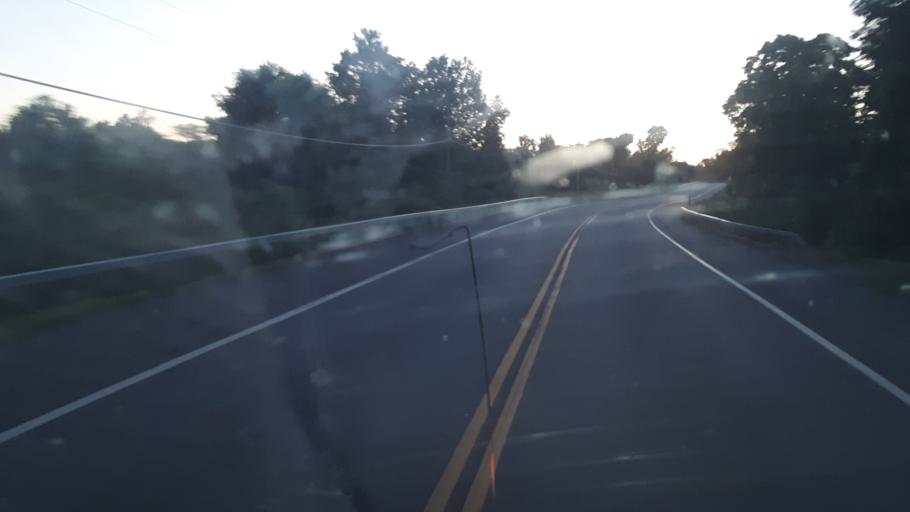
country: US
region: New York
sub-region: Montgomery County
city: Hagaman
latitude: 42.9517
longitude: -74.1198
